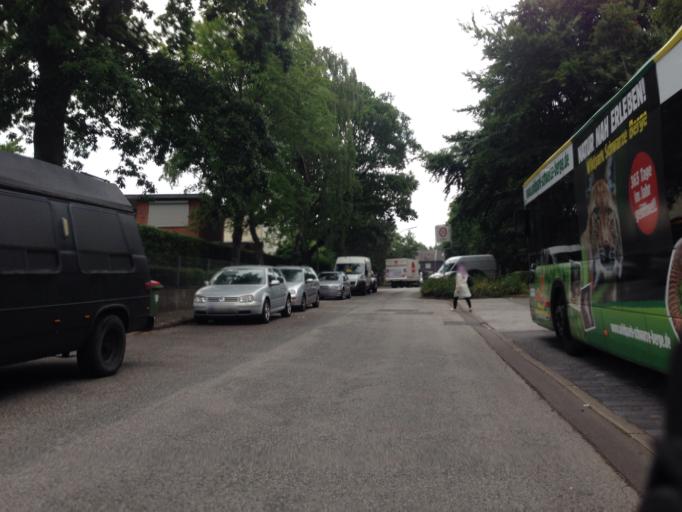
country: DE
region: Schleswig-Holstein
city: Barsbuettel
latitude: 53.5797
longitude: 10.1445
